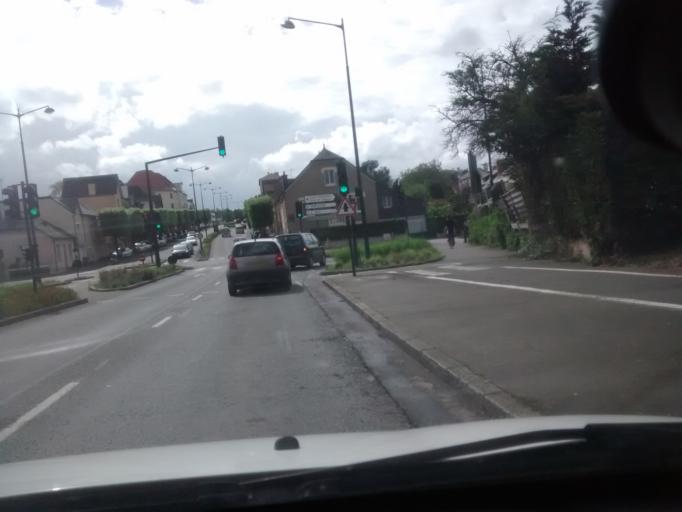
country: FR
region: Brittany
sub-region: Departement d'Ille-et-Vilaine
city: Rennes
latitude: 48.1281
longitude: -1.6827
